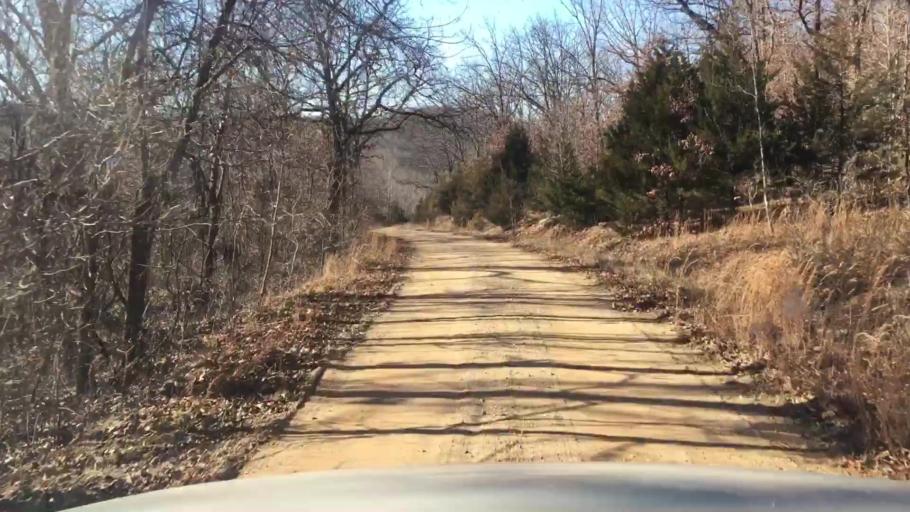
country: US
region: Missouri
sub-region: Camden County
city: Four Seasons
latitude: 38.3199
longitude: -92.7602
